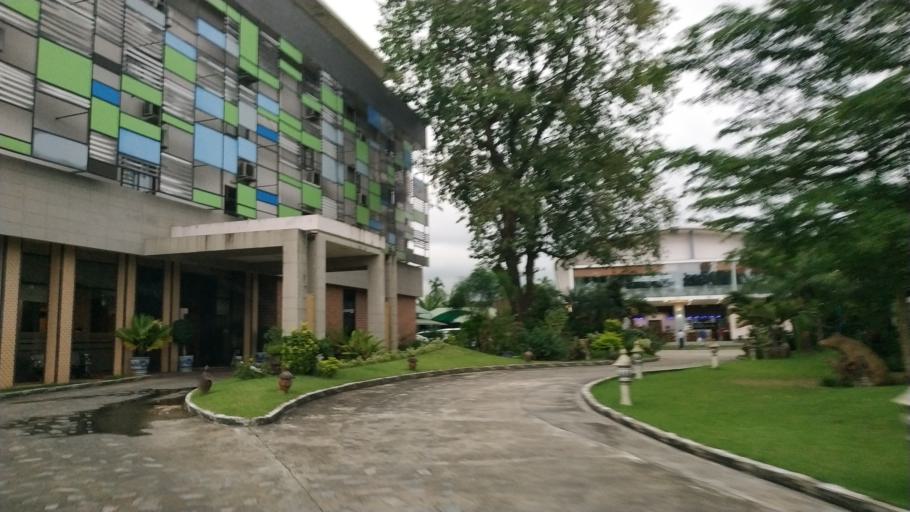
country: MM
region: Tanintharyi
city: Dawei
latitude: 14.0750
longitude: 98.1940
